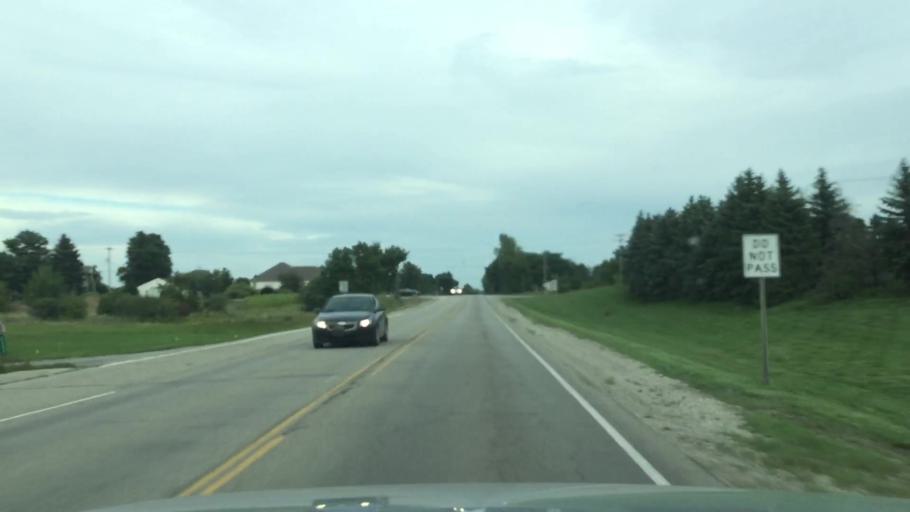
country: US
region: Michigan
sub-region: Genesee County
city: Grand Blanc
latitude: 42.8863
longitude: -83.6577
